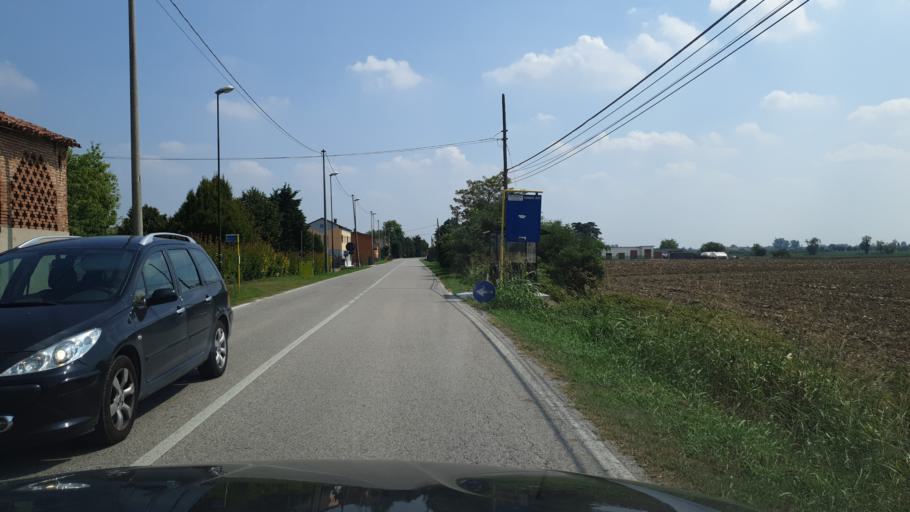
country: IT
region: Veneto
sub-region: Provincia di Rovigo
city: Villamarzana
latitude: 45.0114
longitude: 11.7062
